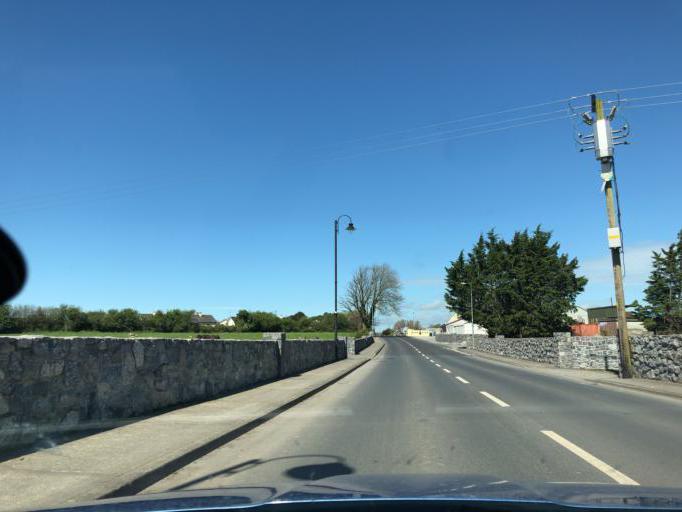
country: IE
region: Connaught
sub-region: County Galway
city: Portumna
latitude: 53.1517
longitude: -8.3751
